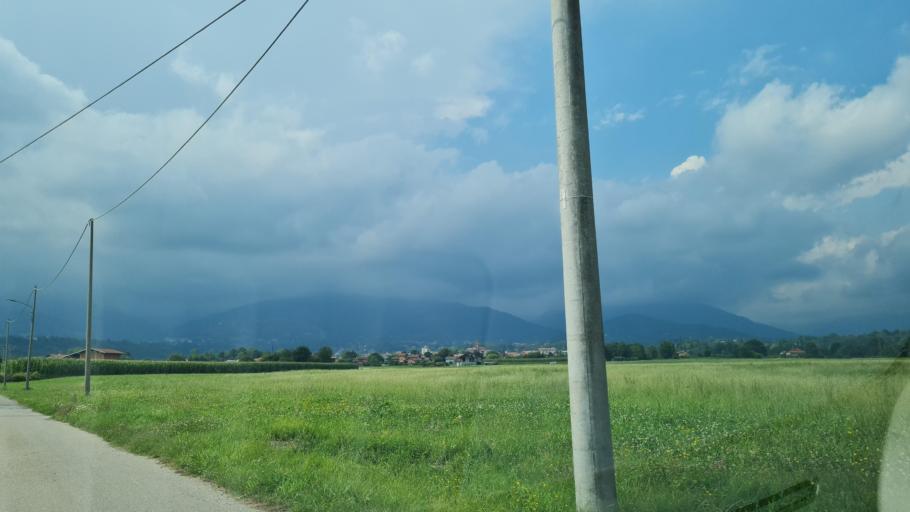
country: IT
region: Piedmont
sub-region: Provincia di Biella
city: Occhieppo Inferiore
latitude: 45.5408
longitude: 8.0309
